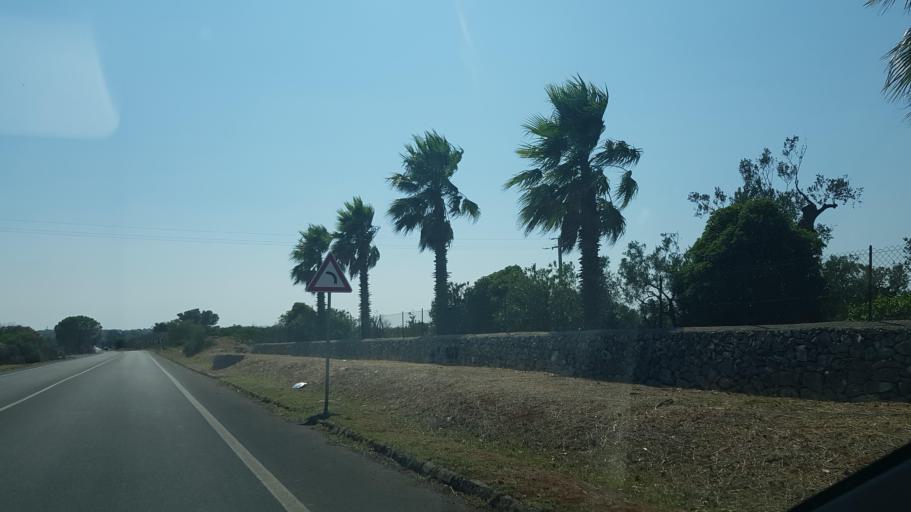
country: IT
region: Apulia
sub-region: Provincia di Lecce
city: Ugento
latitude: 39.9404
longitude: 18.1782
